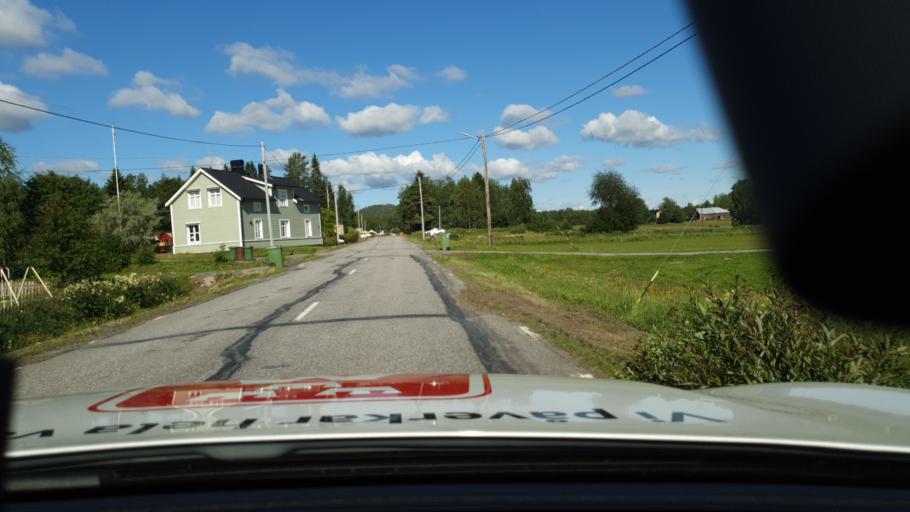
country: SE
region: Norrbotten
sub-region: Lulea Kommun
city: Ranea
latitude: 65.9158
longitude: 22.1608
